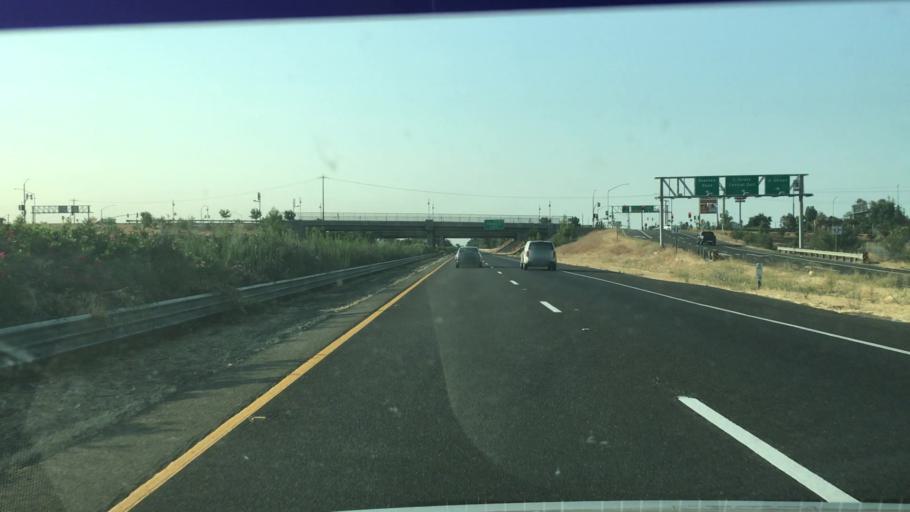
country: US
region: California
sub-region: Sacramento County
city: Galt
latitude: 38.2572
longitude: -121.2955
